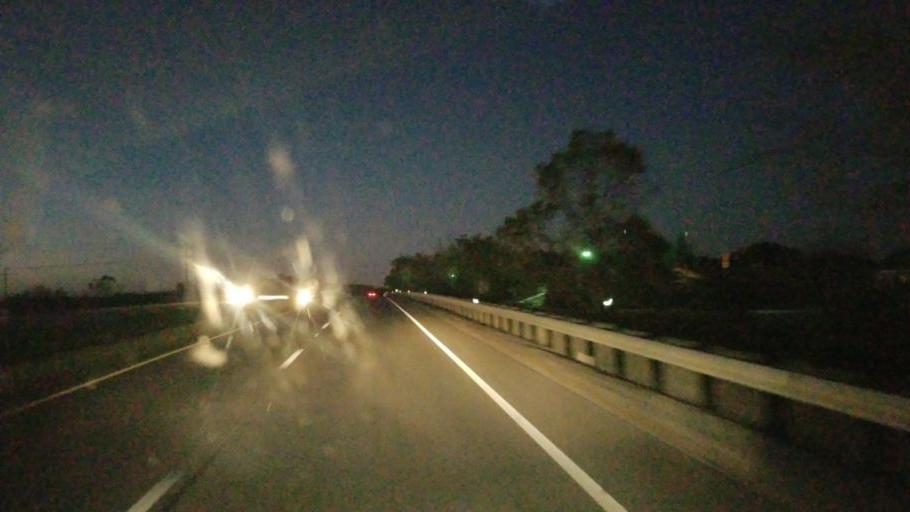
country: US
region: Ohio
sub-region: Pickaway County
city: Circleville
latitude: 39.5903
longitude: -82.9540
